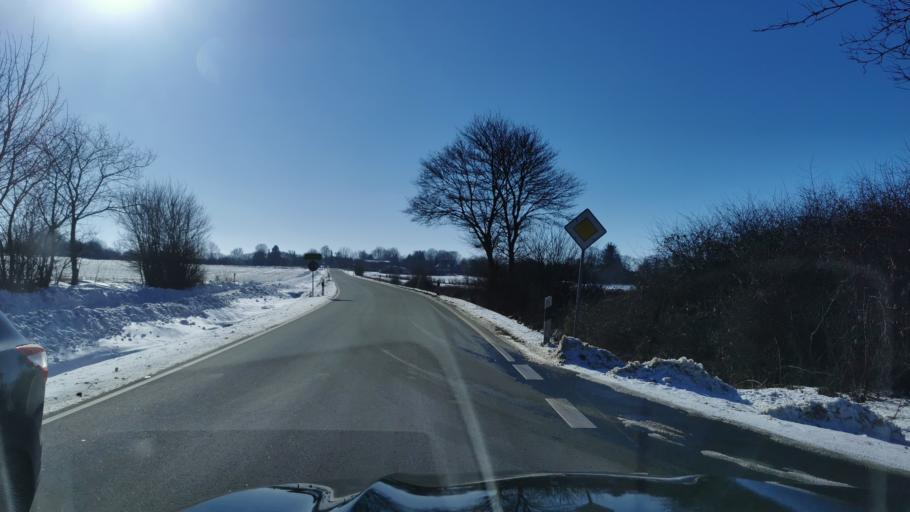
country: DE
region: Schleswig-Holstein
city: Langballig
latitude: 54.8162
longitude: 9.6420
